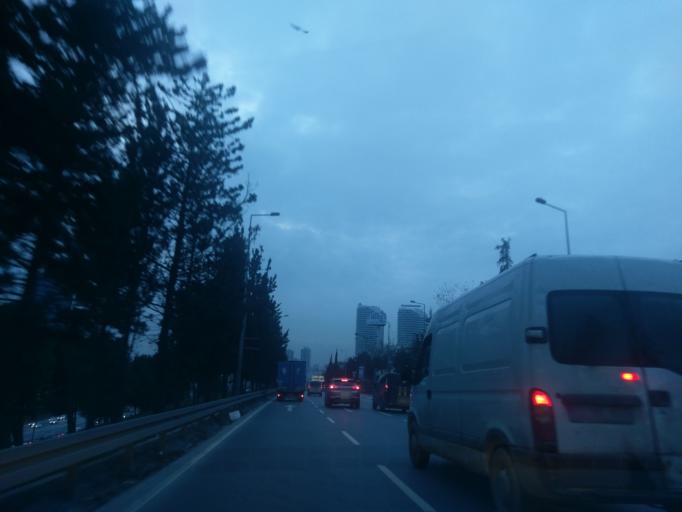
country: TR
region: Istanbul
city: Mahmutbey
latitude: 41.0632
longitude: 28.8191
